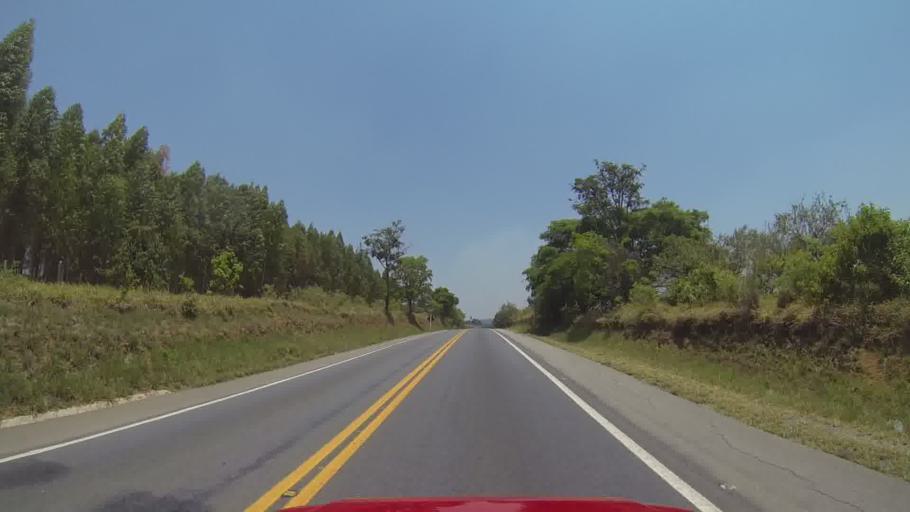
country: BR
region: Minas Gerais
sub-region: Itapecerica
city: Itapecerica
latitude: -20.3081
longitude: -45.2158
